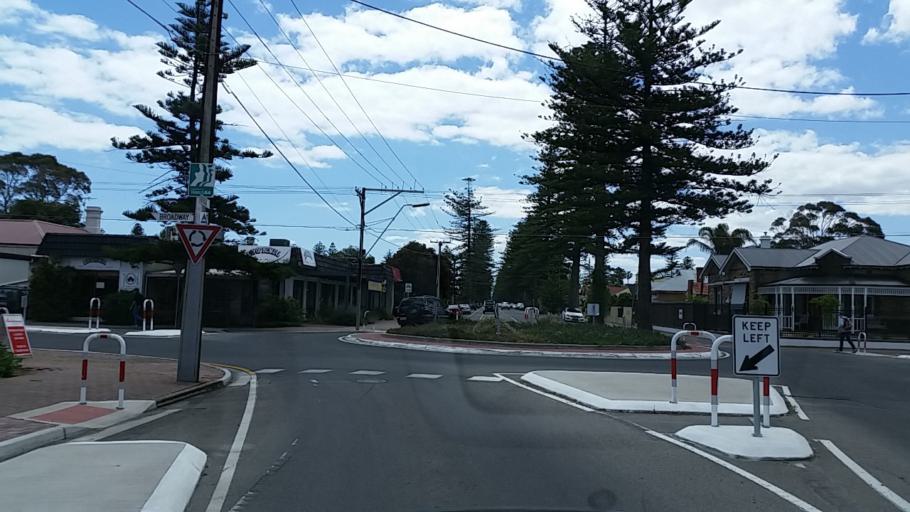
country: AU
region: South Australia
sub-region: Adelaide
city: Glenelg
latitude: -34.9883
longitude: 138.5183
